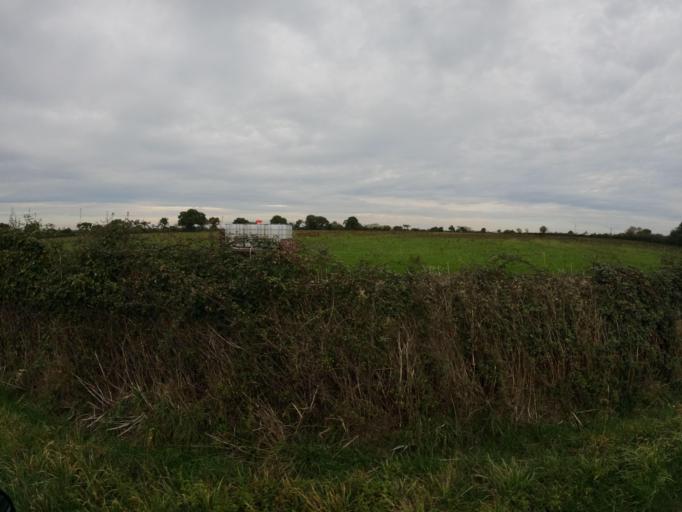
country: FR
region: Pays de la Loire
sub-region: Departement de Maine-et-Loire
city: Saint-Christophe-du-Bois
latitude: 47.0457
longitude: -0.9369
